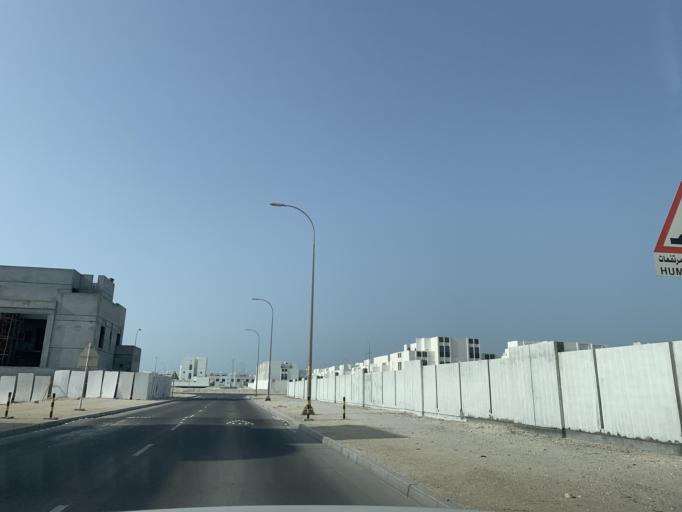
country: BH
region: Muharraq
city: Al Muharraq
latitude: 26.3094
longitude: 50.6352
